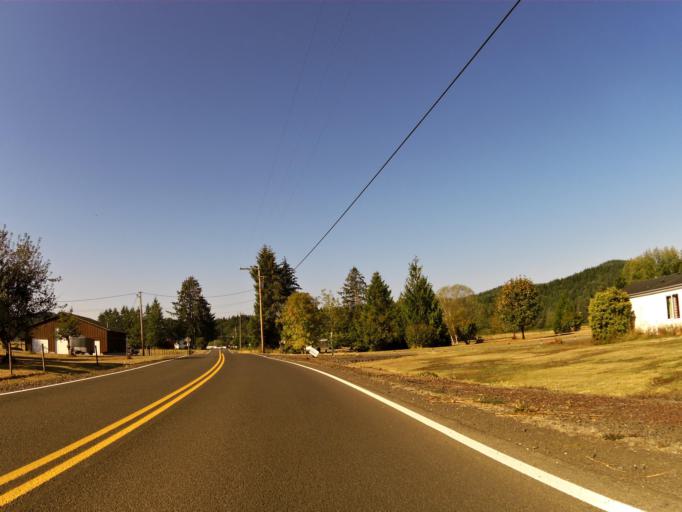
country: US
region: Oregon
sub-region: Tillamook County
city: Tillamook
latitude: 45.3850
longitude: -123.7998
